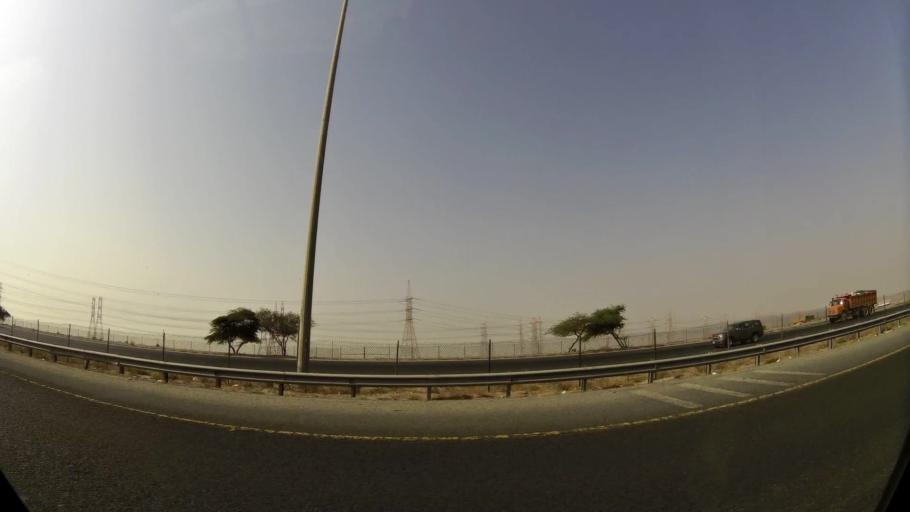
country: KW
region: Al Farwaniyah
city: Al Farwaniyah
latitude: 29.1904
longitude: 47.8843
